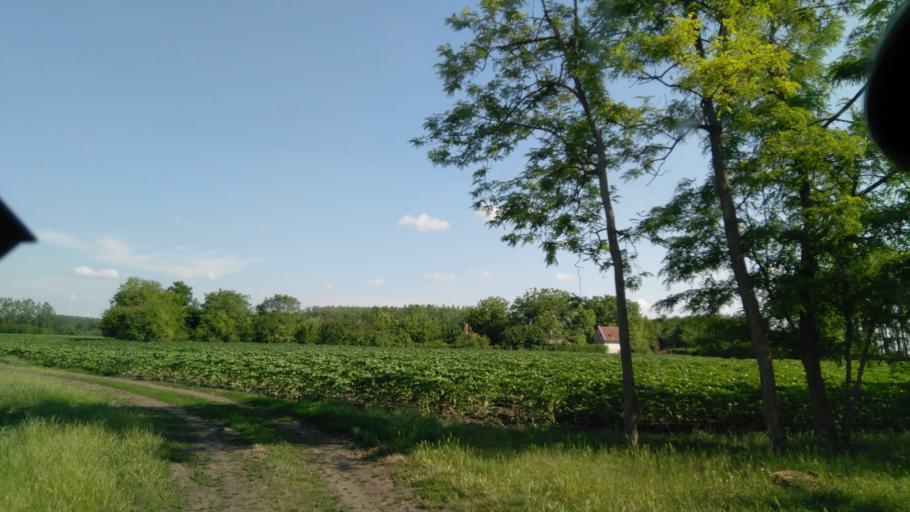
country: HU
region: Bekes
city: Doboz
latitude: 46.7038
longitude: 21.2329
